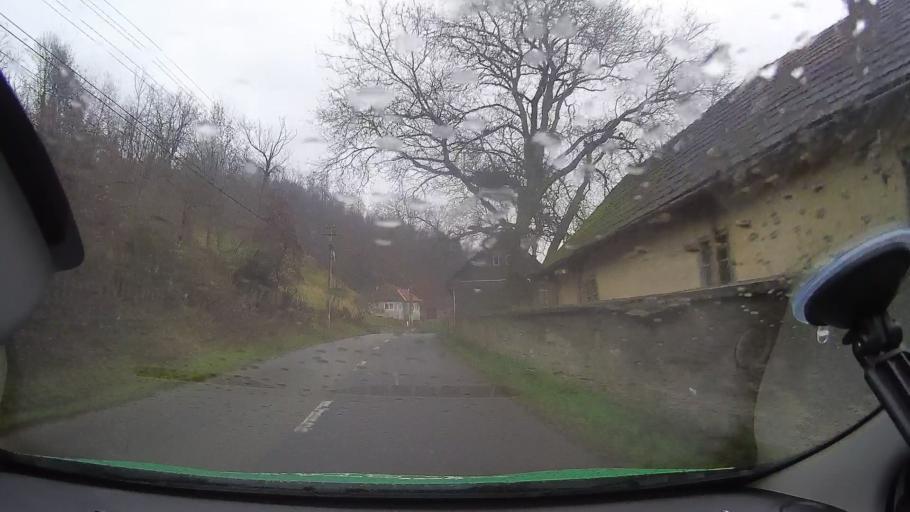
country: RO
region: Hunedoara
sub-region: Comuna Ribita
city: Ribita
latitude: 46.1739
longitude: 22.7682
